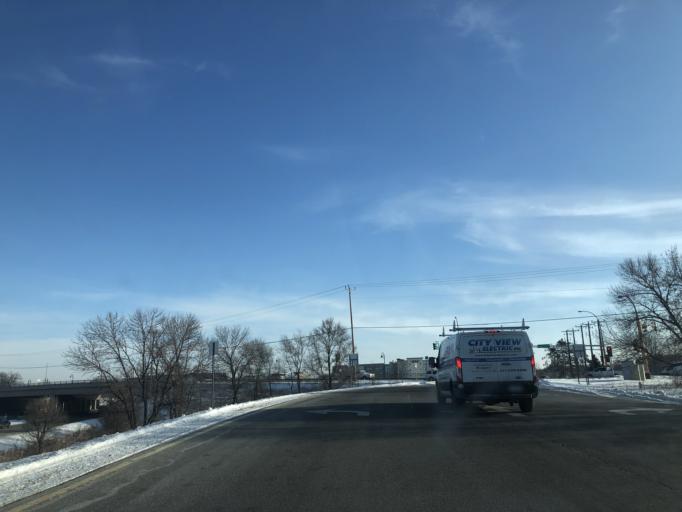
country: US
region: Minnesota
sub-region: Anoka County
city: Lino Lakes
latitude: 45.1791
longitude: -93.1149
